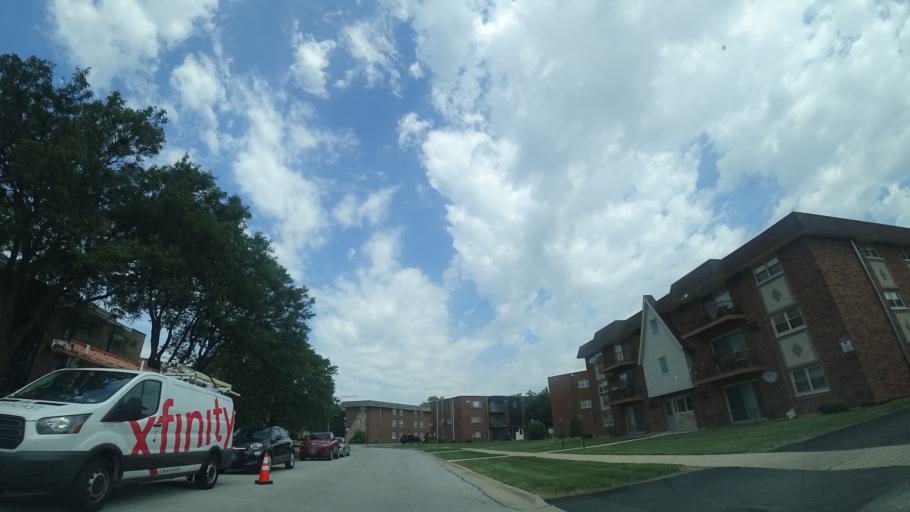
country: US
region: Illinois
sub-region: Cook County
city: Crestwood
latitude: 41.6621
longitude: -87.7564
